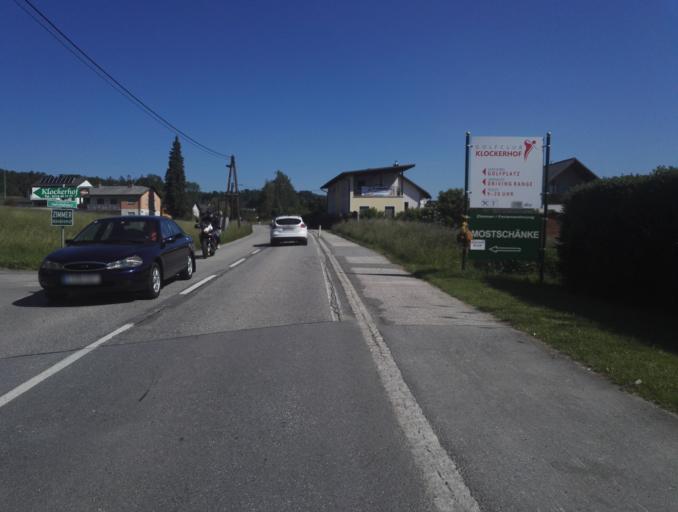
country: AT
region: Styria
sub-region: Politischer Bezirk Graz-Umgebung
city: Hart bei Graz
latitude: 47.0501
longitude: 15.5288
